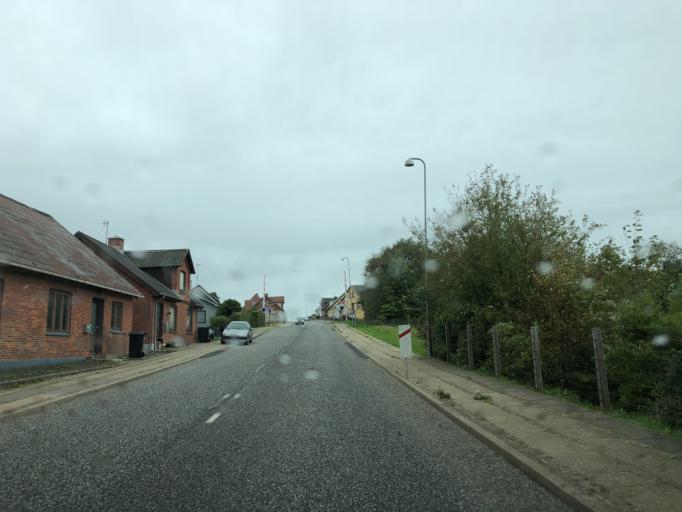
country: DK
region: North Denmark
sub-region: Thisted Kommune
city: Hurup
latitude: 56.7132
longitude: 8.4000
